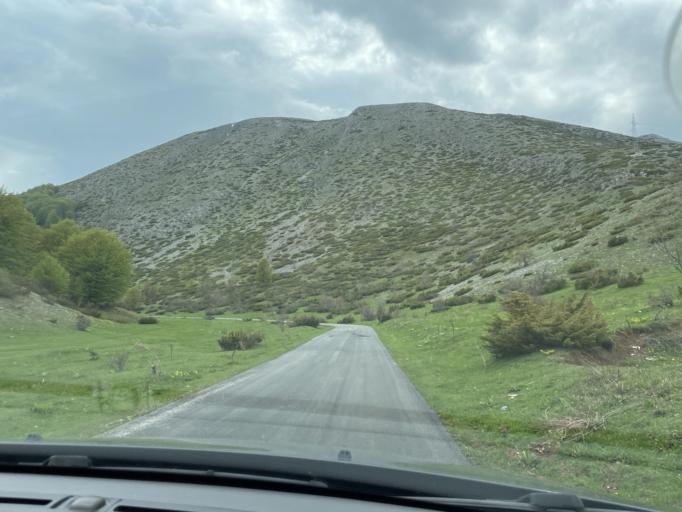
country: MK
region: Opstina Rostusa
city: Rostusha
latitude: 41.6010
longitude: 20.6813
